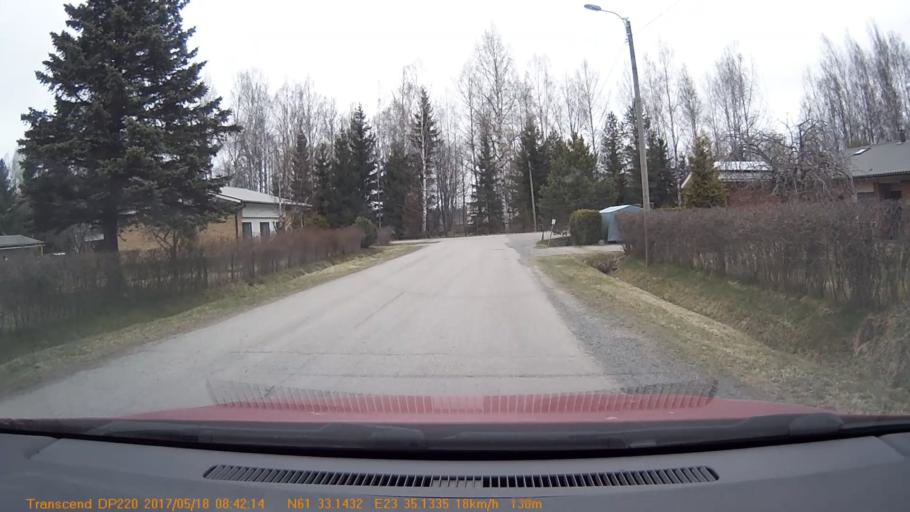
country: FI
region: Pirkanmaa
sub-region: Tampere
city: Yloejaervi
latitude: 61.5523
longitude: 23.5855
